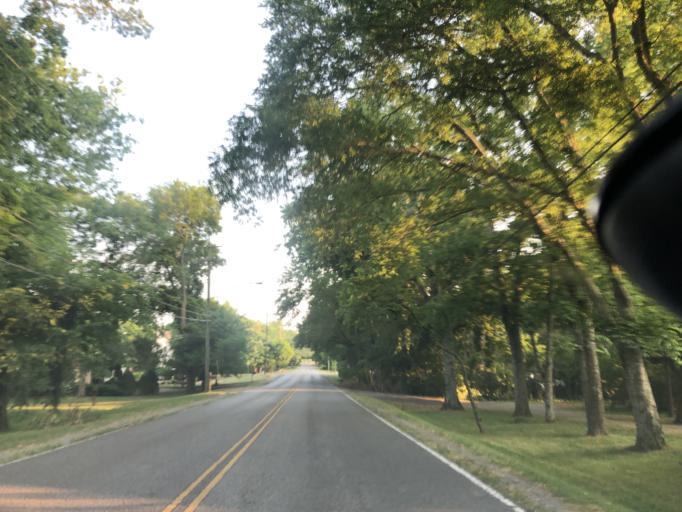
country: US
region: Tennessee
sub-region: Davidson County
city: Oak Hill
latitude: 36.1097
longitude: -86.7880
